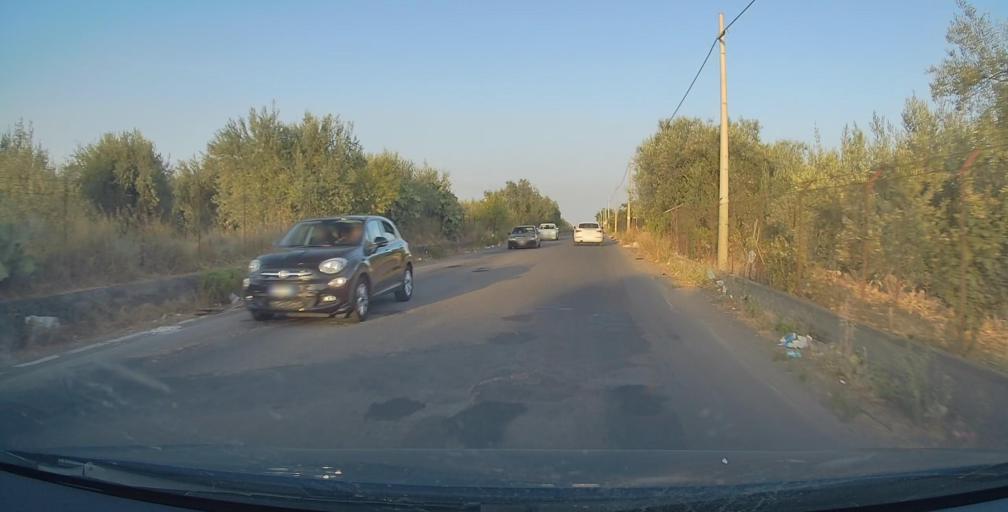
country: IT
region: Sicily
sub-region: Catania
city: Palazzolo
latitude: 37.5489
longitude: 14.9345
